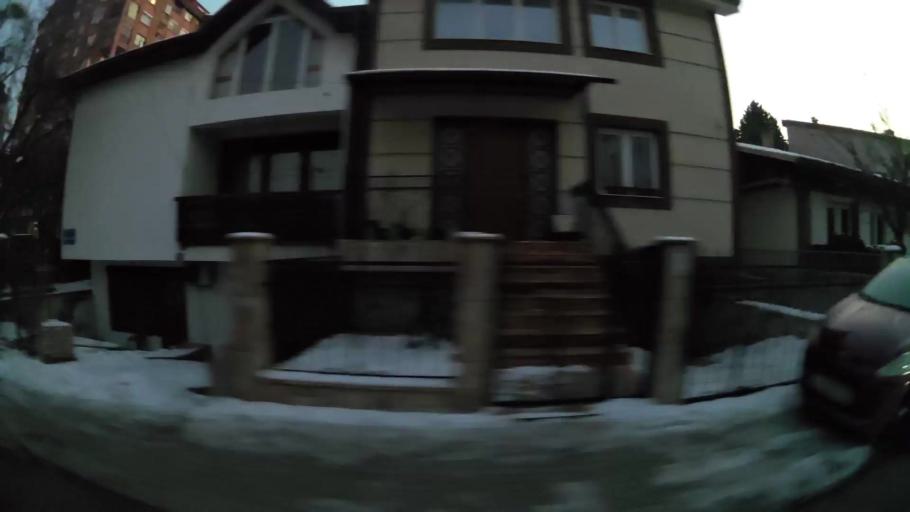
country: MK
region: Karpos
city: Skopje
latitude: 41.9977
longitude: 21.4081
